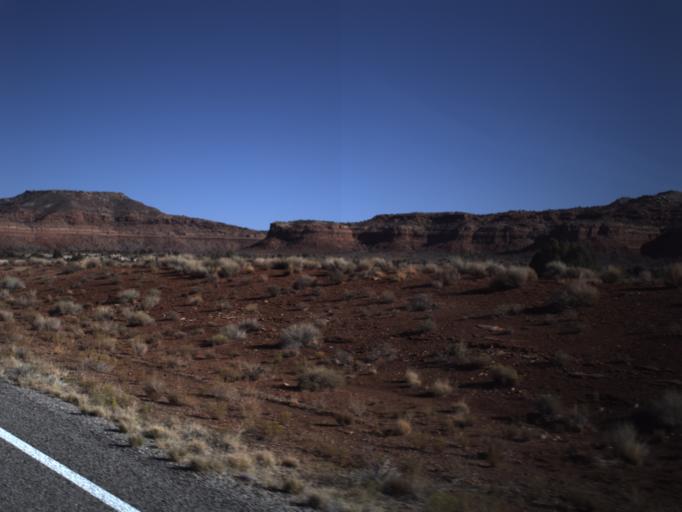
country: US
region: Utah
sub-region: San Juan County
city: Blanding
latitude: 37.7109
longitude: -110.2425
